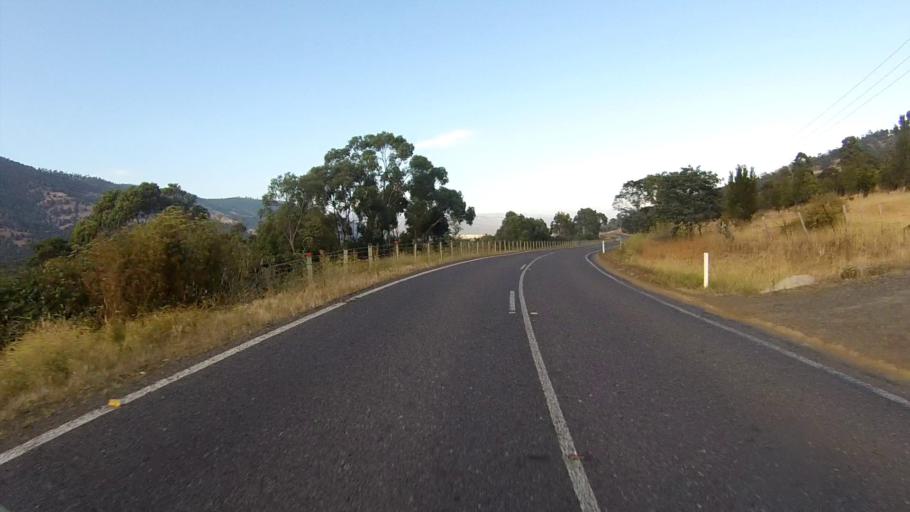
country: AU
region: Tasmania
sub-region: Glenorchy
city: Granton
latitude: -42.7503
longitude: 147.1521
